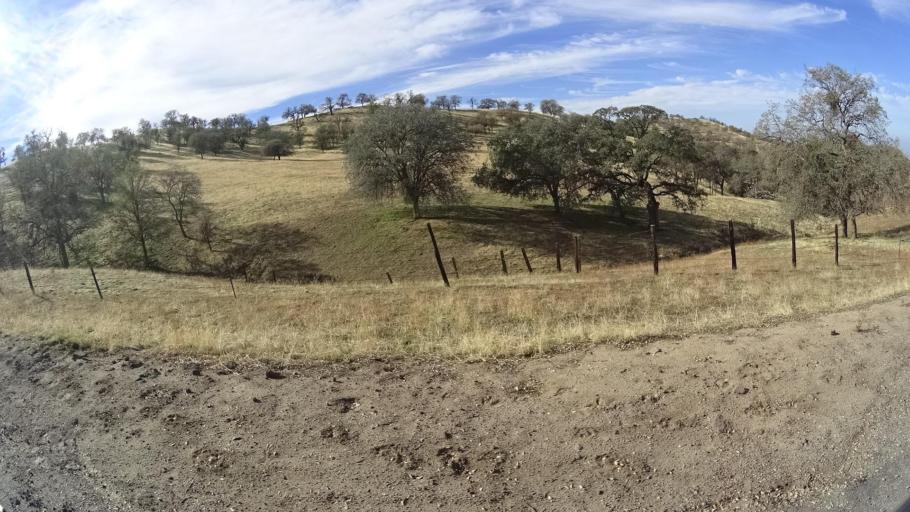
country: US
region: California
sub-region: Kern County
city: Oildale
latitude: 35.5717
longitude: -118.8001
